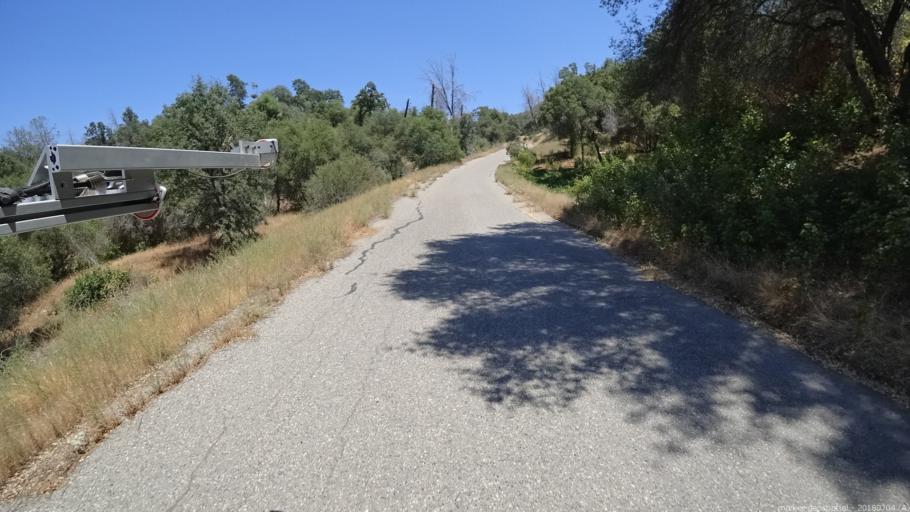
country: US
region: California
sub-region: Madera County
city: Coarsegold
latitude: 37.1826
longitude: -119.6199
